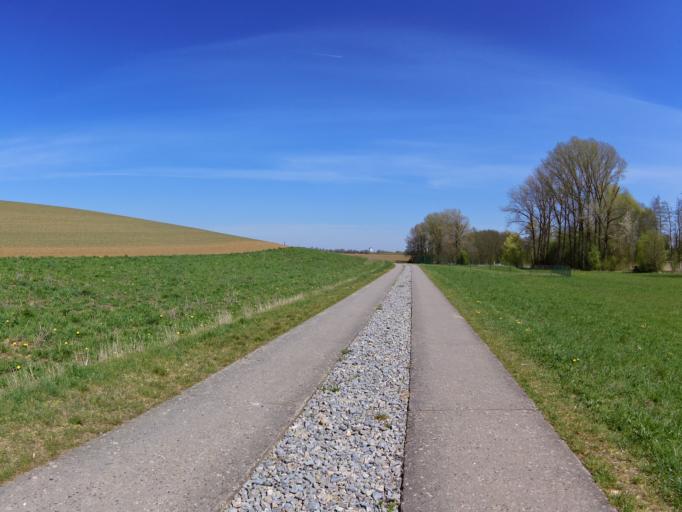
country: DE
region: Bavaria
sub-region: Regierungsbezirk Unterfranken
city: Kurnach
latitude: 49.8610
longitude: 10.0216
